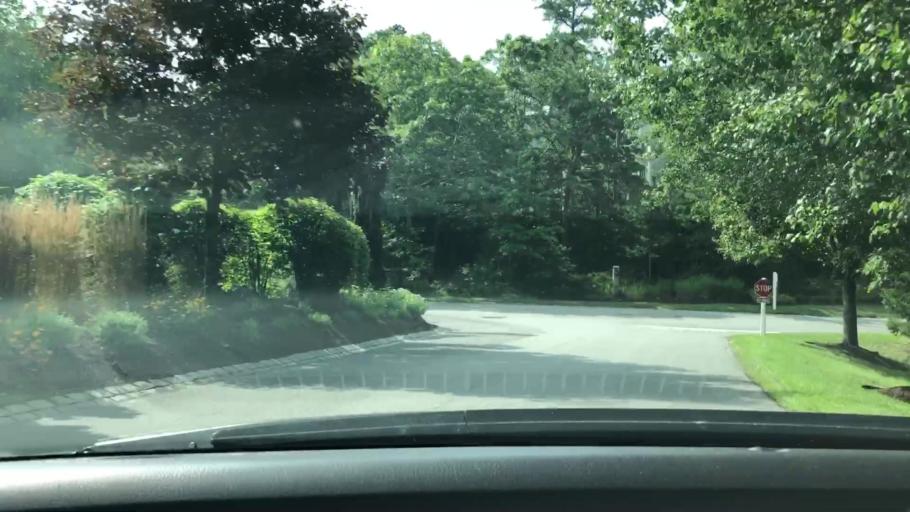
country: US
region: Massachusetts
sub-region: Plymouth County
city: White Island Shores
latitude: 41.8827
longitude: -70.6023
